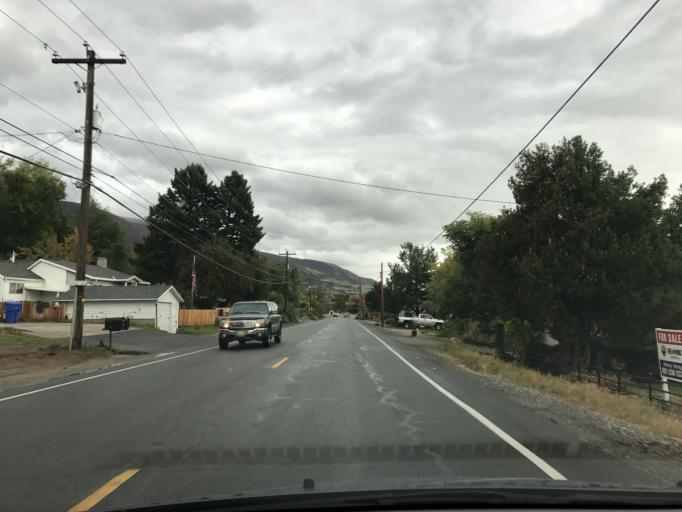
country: US
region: Utah
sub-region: Davis County
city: Farmington
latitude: 40.9937
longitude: -111.8951
